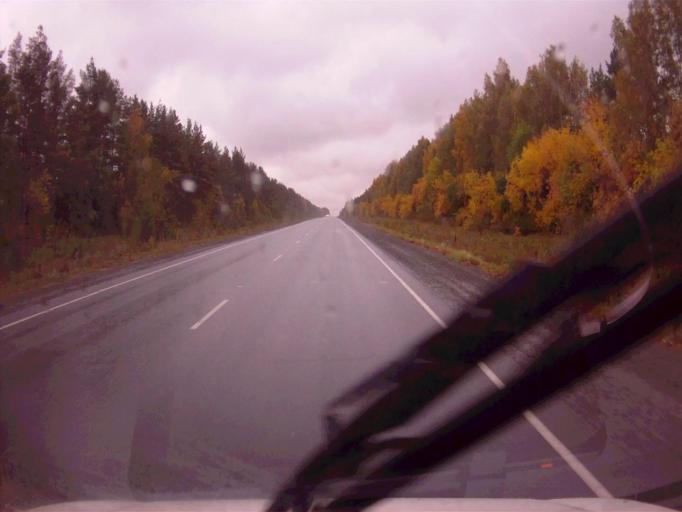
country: RU
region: Chelyabinsk
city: Roshchino
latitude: 55.3759
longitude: 61.1502
